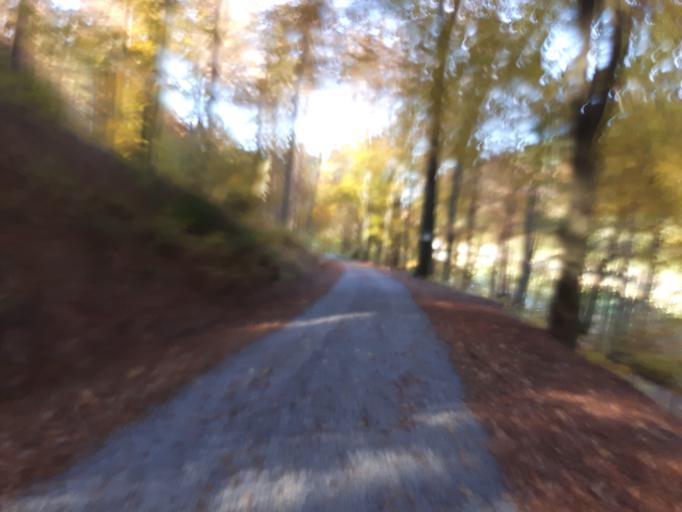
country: DE
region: Bavaria
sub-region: Regierungsbezirk Unterfranken
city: Heimbuchenthal
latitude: 49.8983
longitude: 9.3028
